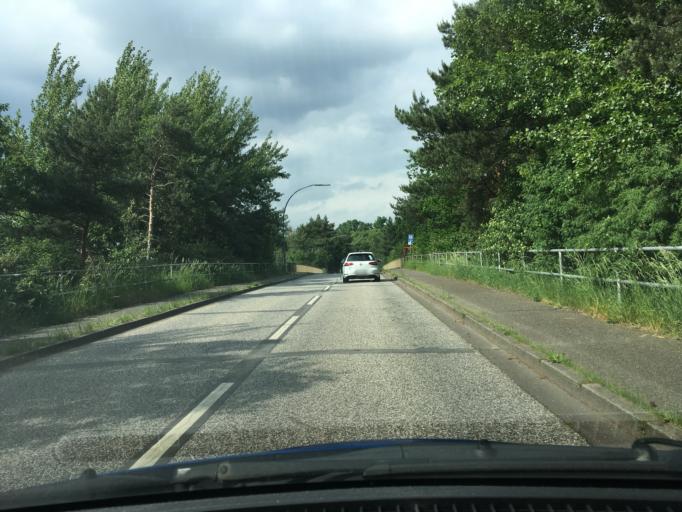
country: DE
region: Hamburg
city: Bergedorf
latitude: 53.4761
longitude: 10.2313
